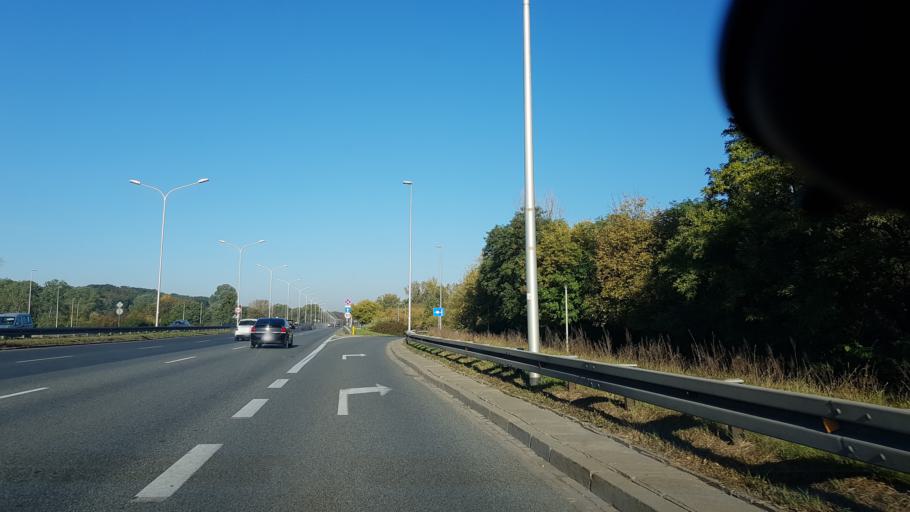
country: PL
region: Masovian Voivodeship
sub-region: Warszawa
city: Zoliborz
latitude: 52.2900
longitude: 20.9788
